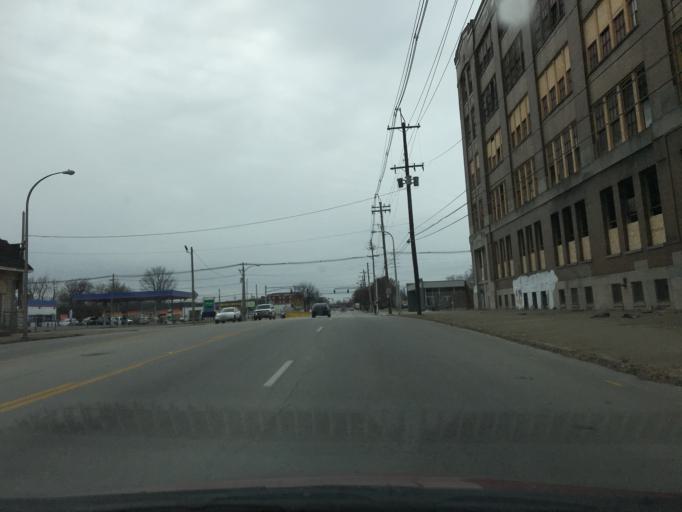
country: US
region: Kentucky
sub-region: Jefferson County
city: Louisville
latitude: 38.2481
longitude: -85.7750
